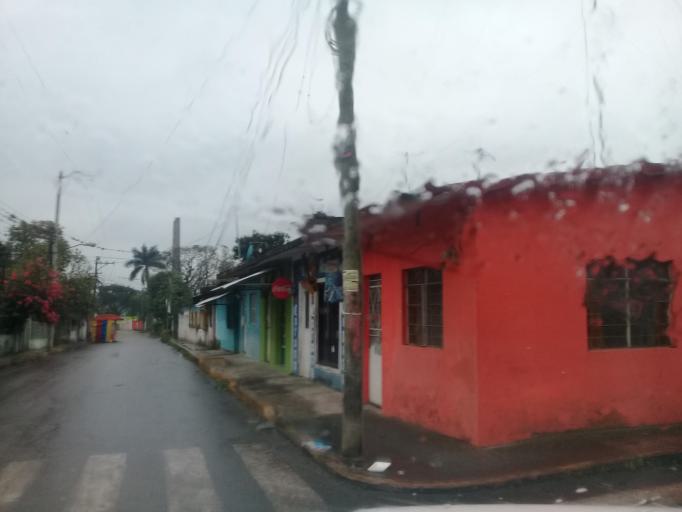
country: MX
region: Veracruz
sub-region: Cordoba
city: San Jose de Tapia
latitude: 18.8485
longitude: -96.9499
